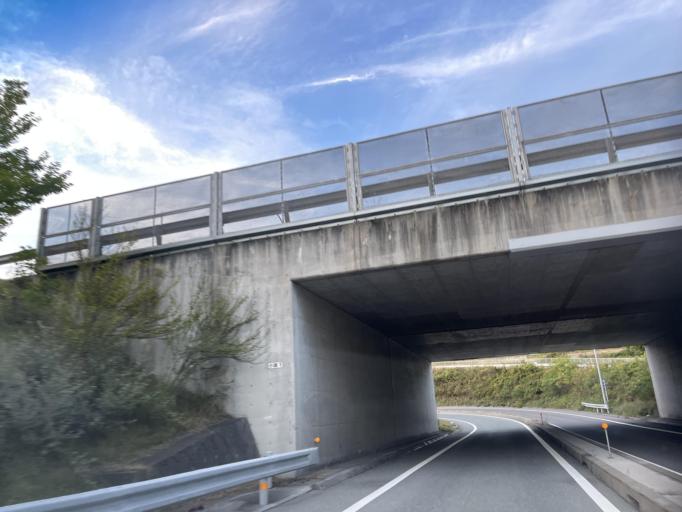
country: JP
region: Nagano
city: Komoro
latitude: 36.3456
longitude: 138.4075
